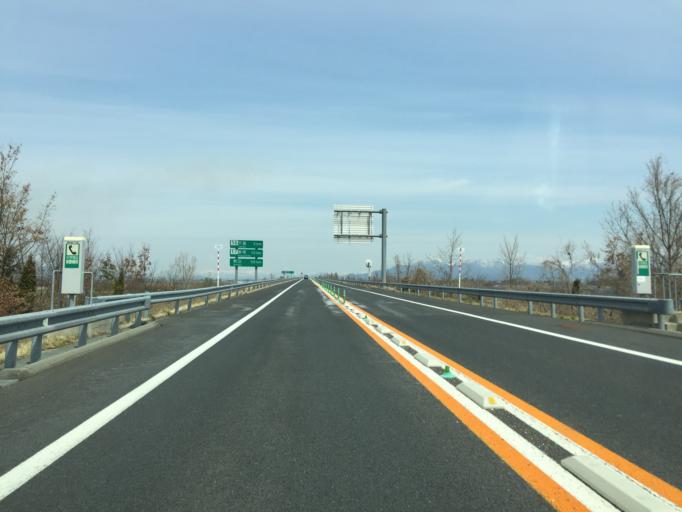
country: JP
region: Yamagata
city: Tendo
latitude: 38.3218
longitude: 140.3255
